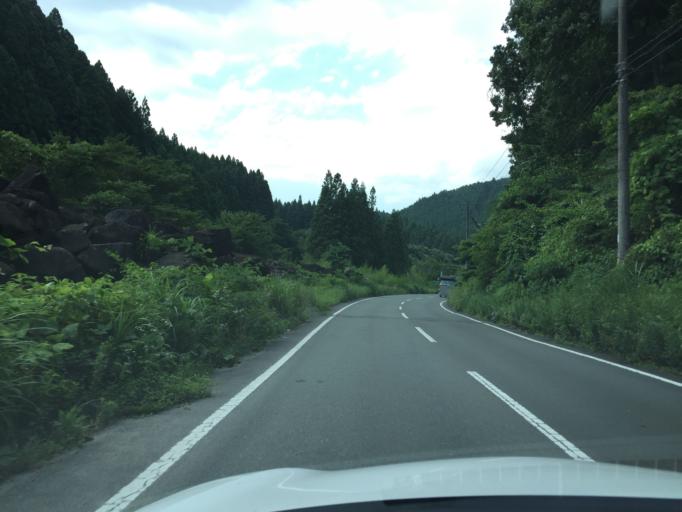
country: JP
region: Fukushima
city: Iwaki
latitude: 37.0045
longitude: 140.7188
